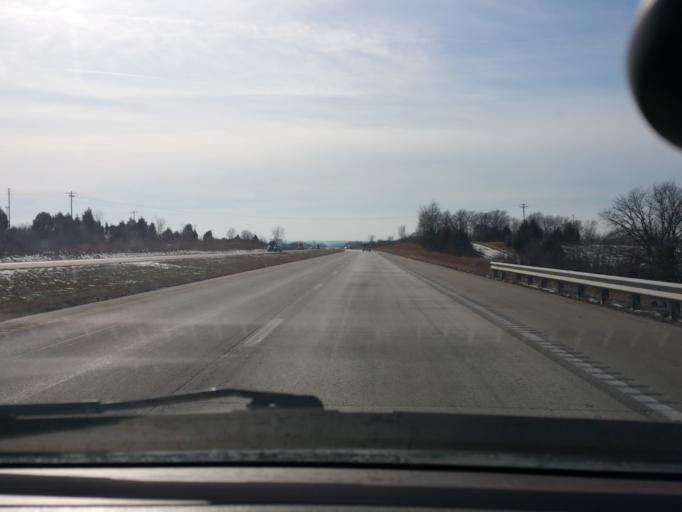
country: US
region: Missouri
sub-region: Clay County
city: Kearney
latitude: 39.4525
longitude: -94.3257
